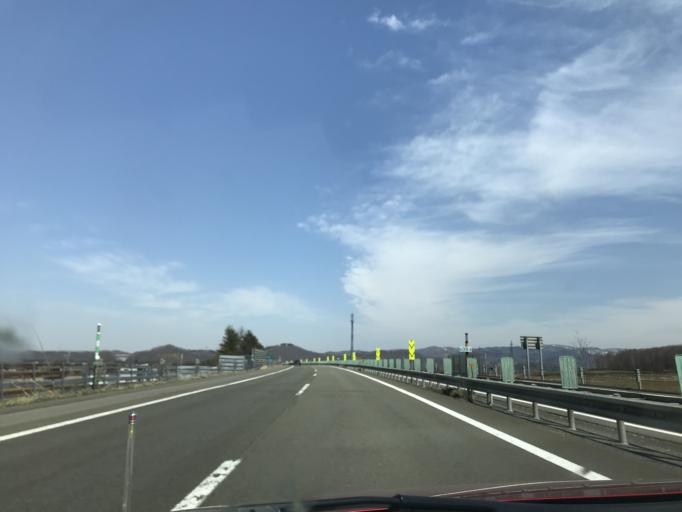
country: JP
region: Hokkaido
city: Iwamizawa
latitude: 43.2223
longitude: 141.8287
